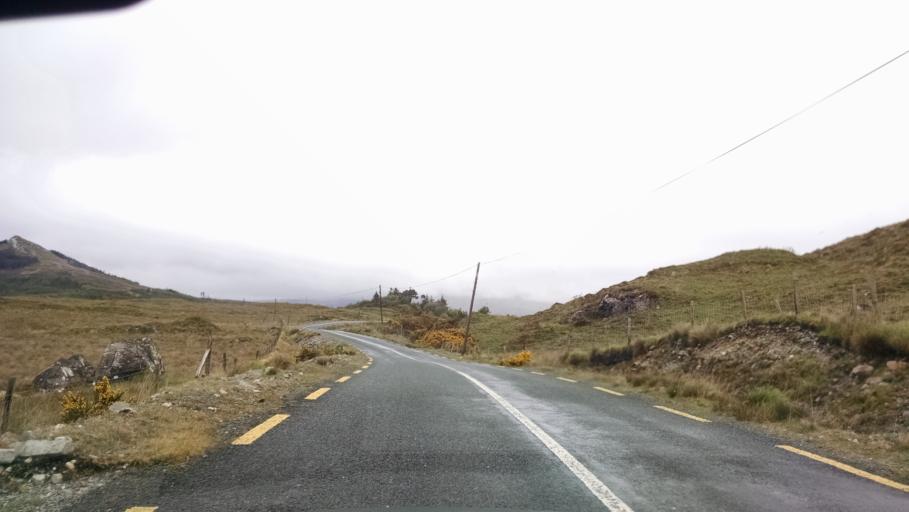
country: IE
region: Connaught
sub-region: County Galway
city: Clifden
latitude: 53.4791
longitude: -9.7416
